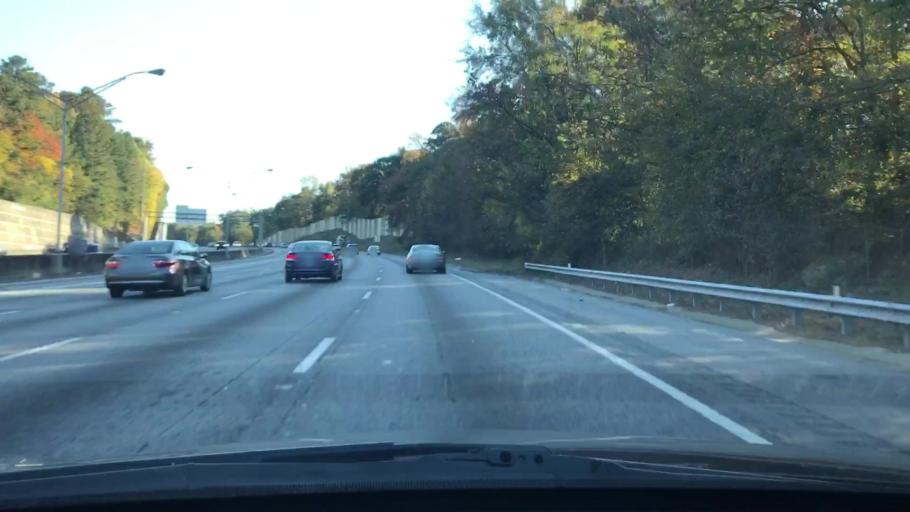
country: US
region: Georgia
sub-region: Cobb County
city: Vinings
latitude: 33.8418
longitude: -84.4302
